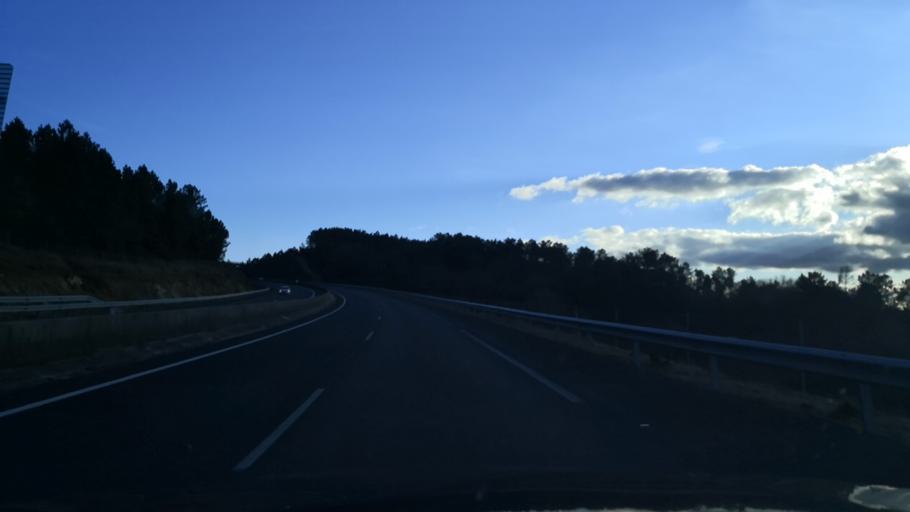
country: ES
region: Galicia
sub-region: Provincia de Pontevedra
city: Lalin
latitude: 42.6123
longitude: -8.1004
